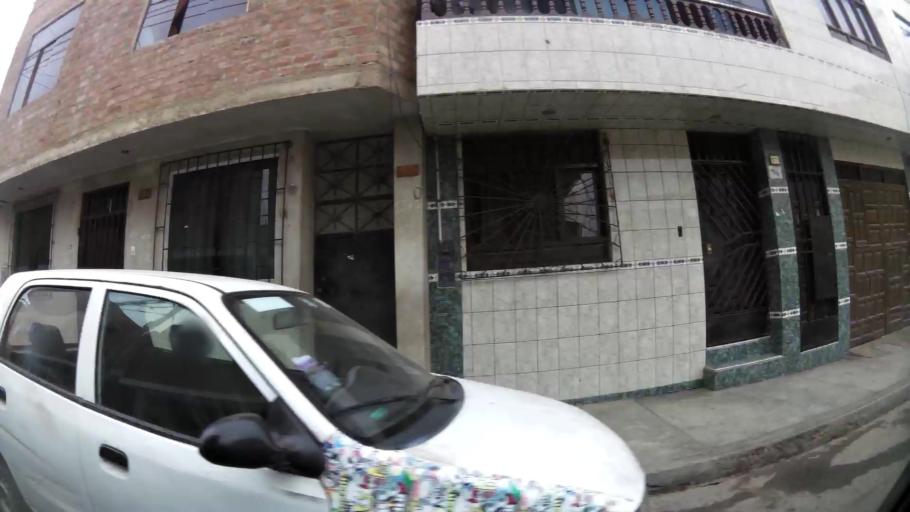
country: PE
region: La Libertad
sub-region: Provincia de Trujillo
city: La Esperanza
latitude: -8.0820
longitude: -79.0458
